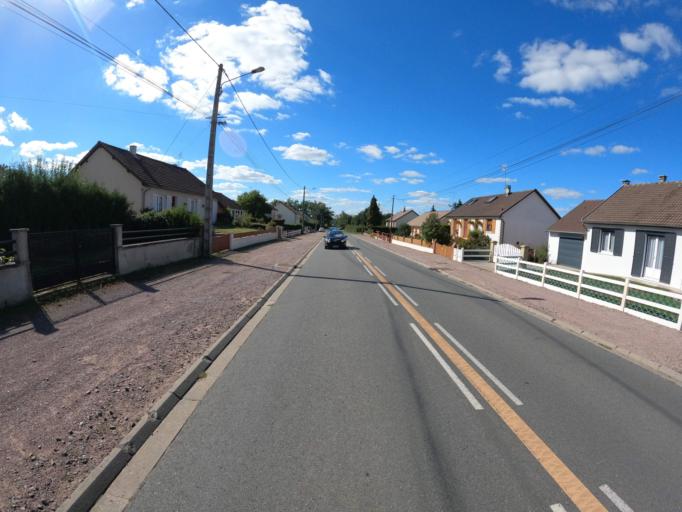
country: FR
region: Auvergne
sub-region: Departement de l'Allier
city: Doyet
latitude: 46.3971
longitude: 2.8515
